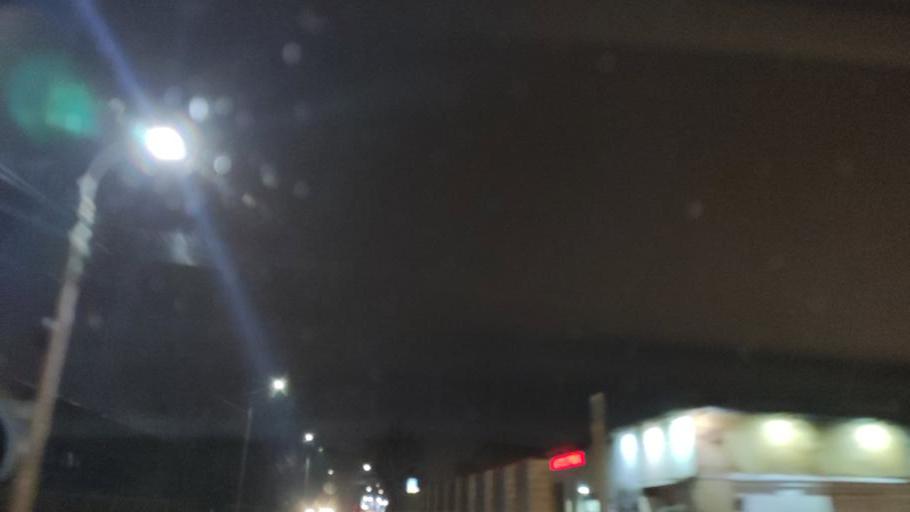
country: RU
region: Moskovskaya
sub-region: Podol'skiy Rayon
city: Podol'sk
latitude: 55.4390
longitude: 37.5803
